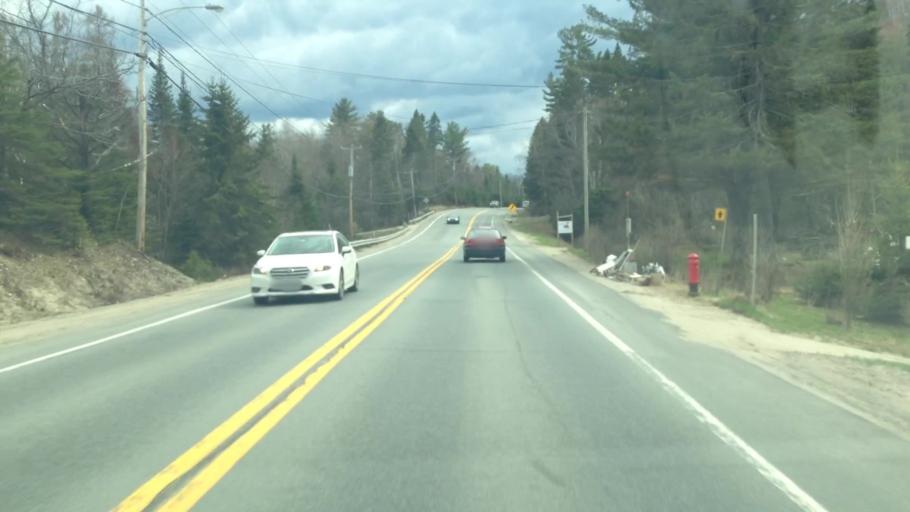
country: CA
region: Quebec
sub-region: Laurentides
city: Sainte-Adele
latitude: 45.9989
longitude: -74.1116
